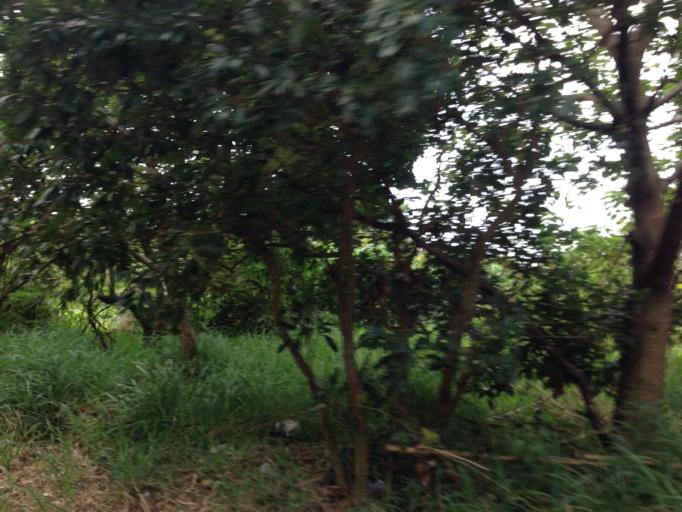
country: TW
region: Taiwan
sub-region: Hsinchu
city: Hsinchu
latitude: 24.7498
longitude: 120.9560
